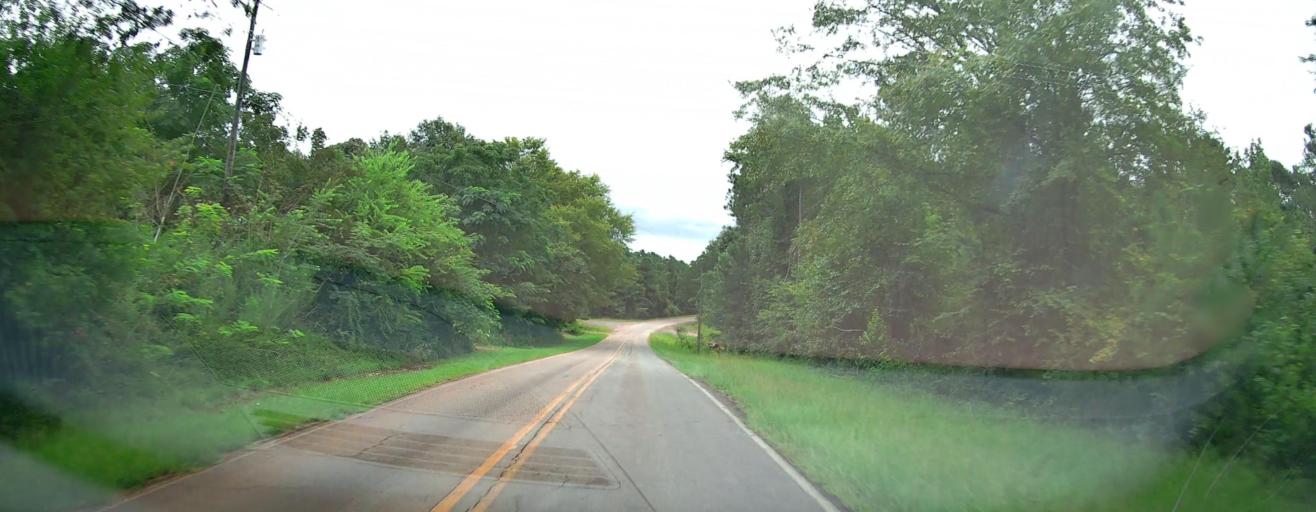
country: US
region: Georgia
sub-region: Bibb County
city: Macon
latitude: 32.7742
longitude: -83.5101
